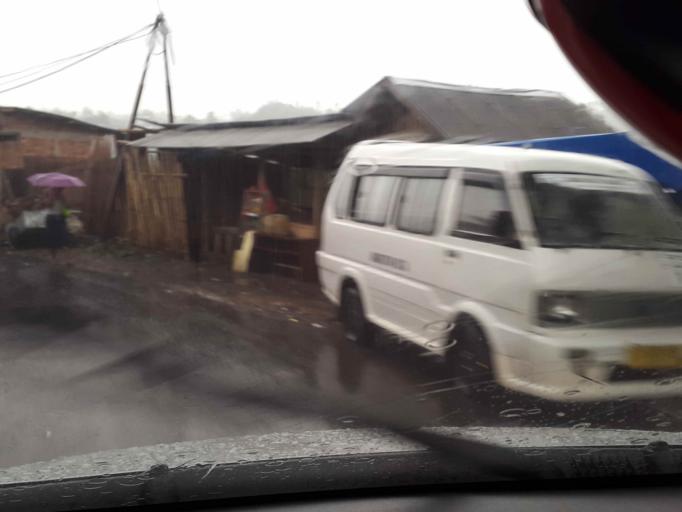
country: ID
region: West Java
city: Sukabumi
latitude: -6.8907
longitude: 106.9231
